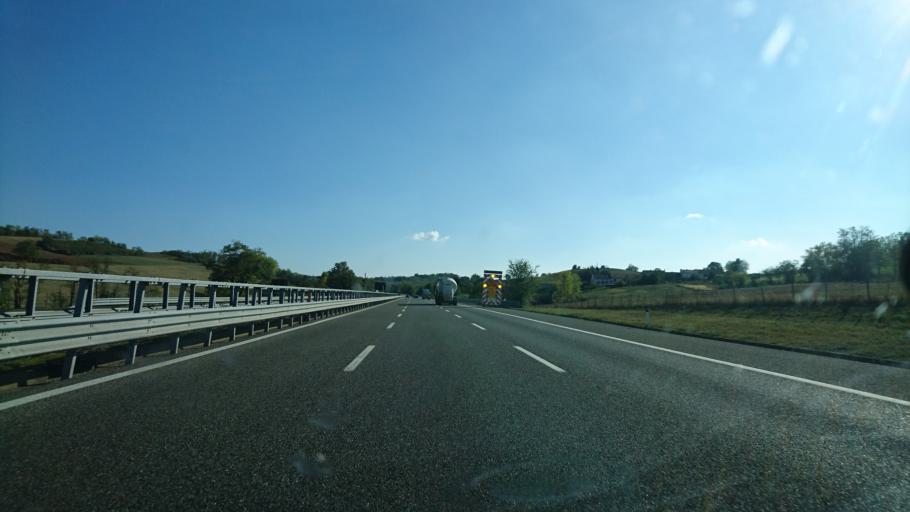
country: IT
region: Piedmont
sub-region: Provincia di Alessandria
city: Mirabello Monferrato
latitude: 45.0135
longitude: 8.5349
